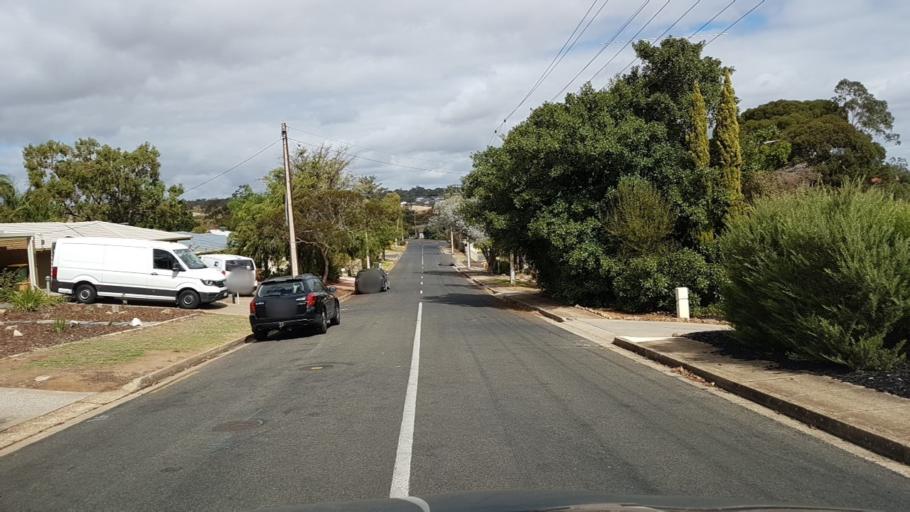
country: AU
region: South Australia
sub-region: Gawler
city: Gawler
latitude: -34.6072
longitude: 138.7542
